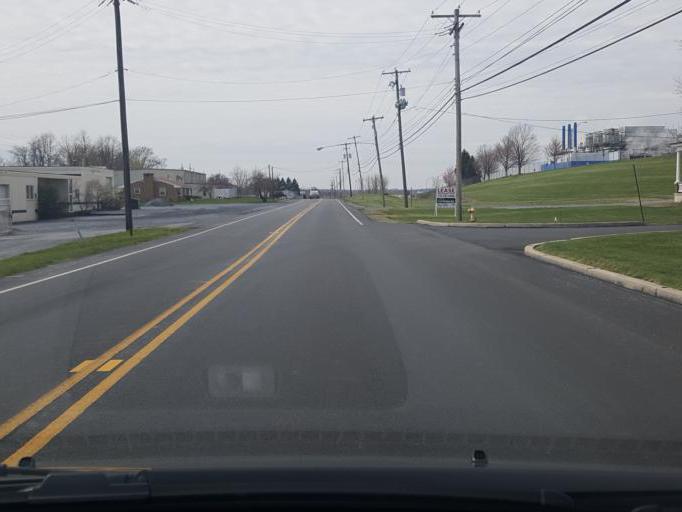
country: US
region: Pennsylvania
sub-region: Dauphin County
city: Hershey
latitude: 40.2776
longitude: -76.6716
